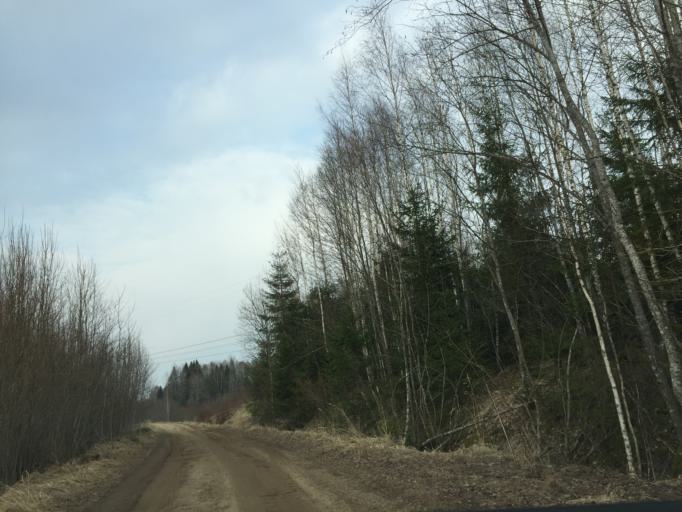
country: LV
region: Priekuli
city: Priekuli
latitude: 57.2081
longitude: 25.4017
